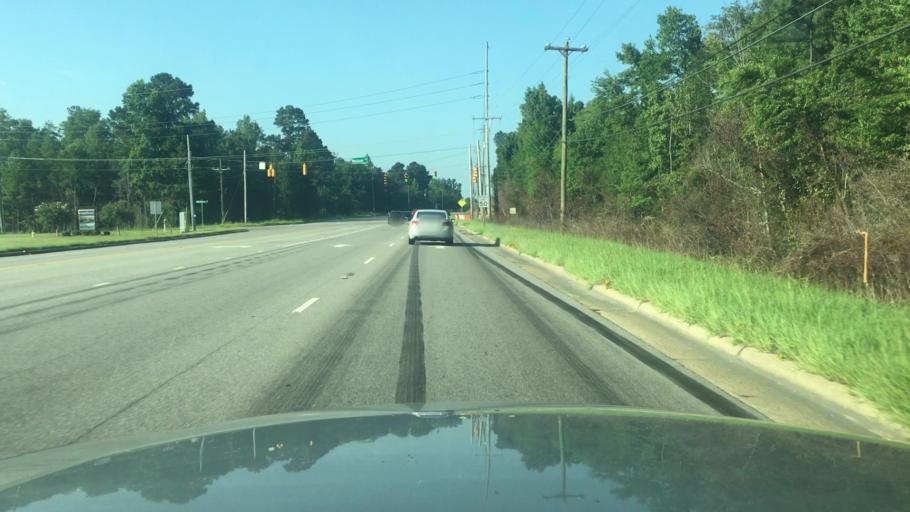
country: US
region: North Carolina
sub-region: Cumberland County
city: Eastover
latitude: 35.1689
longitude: -78.8622
